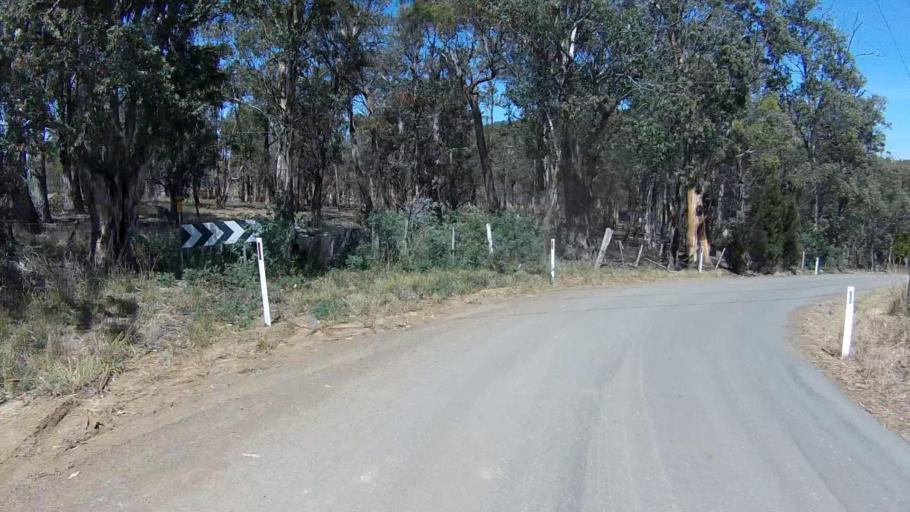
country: AU
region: Tasmania
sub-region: Sorell
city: Sorell
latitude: -42.7833
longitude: 147.6433
